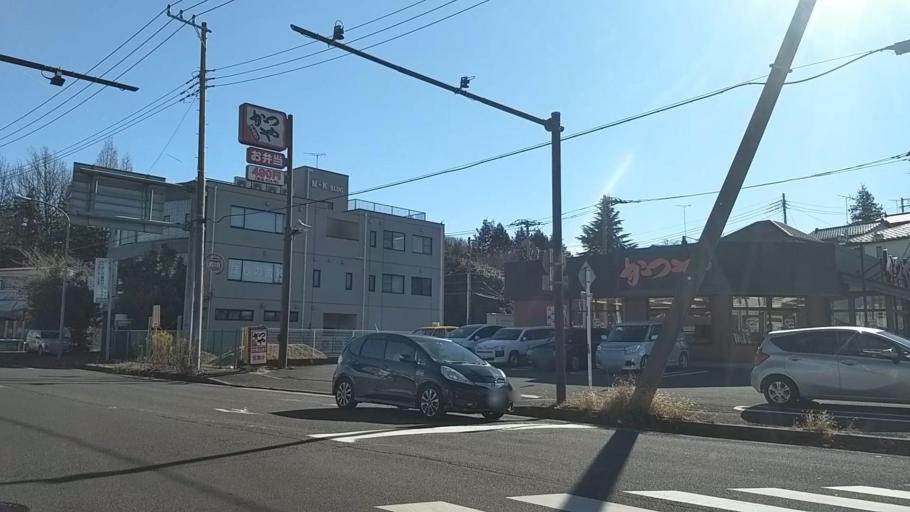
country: JP
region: Kanagawa
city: Yokohama
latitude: 35.4636
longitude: 139.5641
